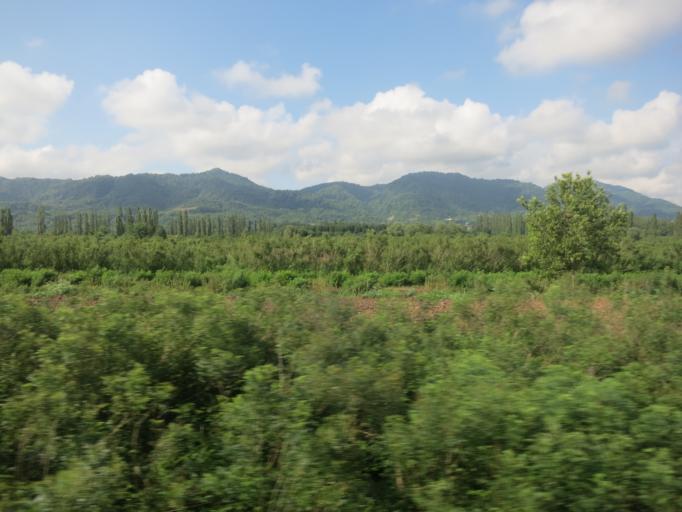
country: GE
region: Guria
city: Lanchkhuti
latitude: 42.0860
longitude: 42.0661
